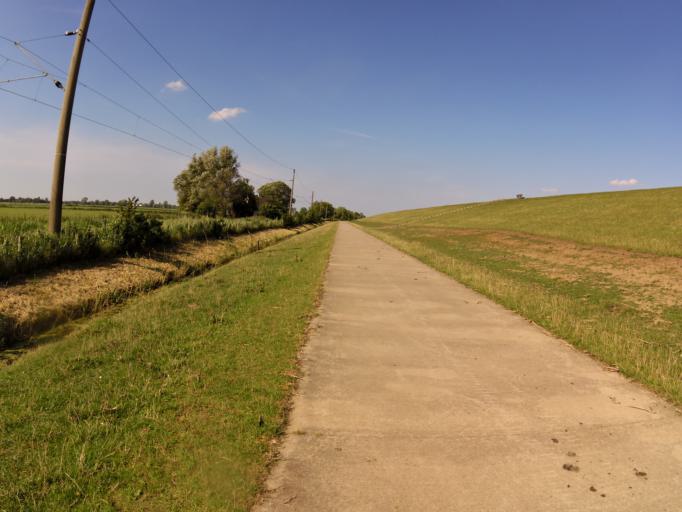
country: DE
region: Lower Saxony
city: Nordenham
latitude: 53.4527
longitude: 8.4751
